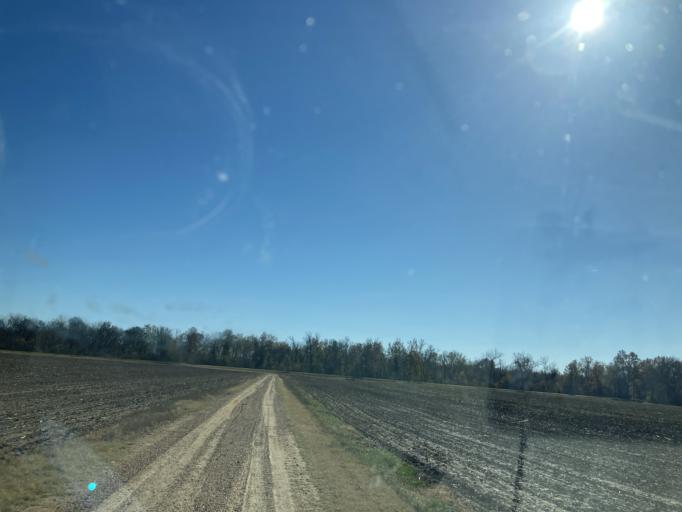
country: US
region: Mississippi
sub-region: Yazoo County
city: Yazoo City
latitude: 32.8993
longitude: -90.4496
